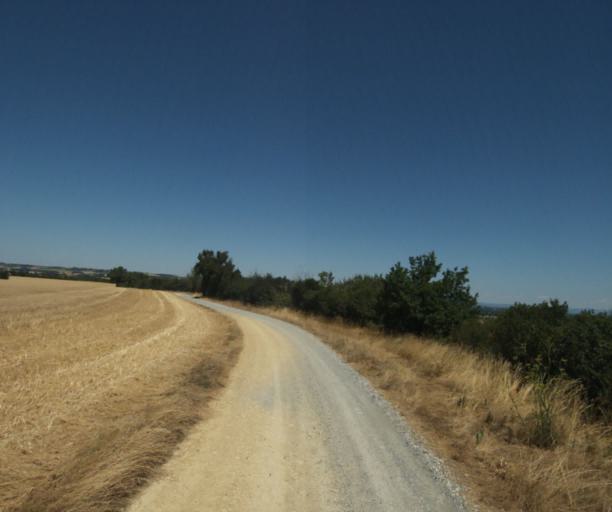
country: FR
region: Midi-Pyrenees
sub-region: Departement de la Haute-Garonne
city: Saint-Felix-Lauragais
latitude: 43.4643
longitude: 1.9208
